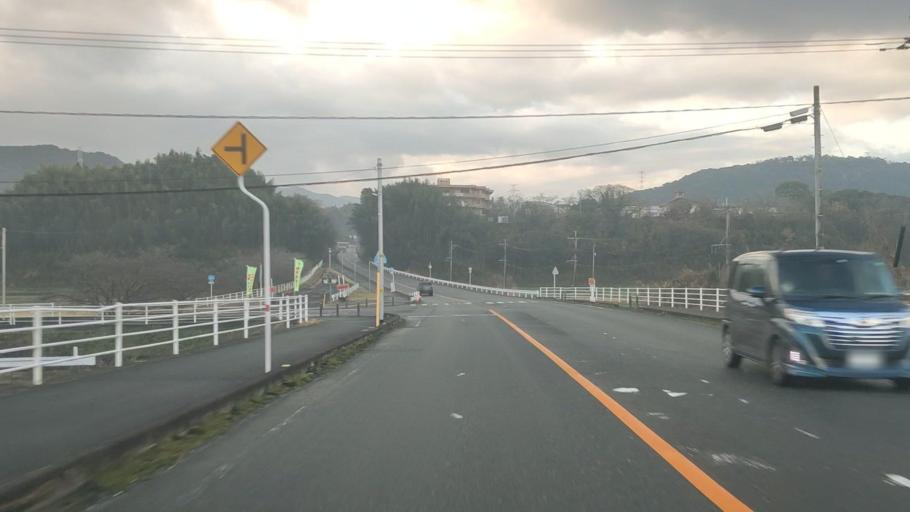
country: JP
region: Kumamoto
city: Matsubase
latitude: 32.6413
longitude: 130.8128
